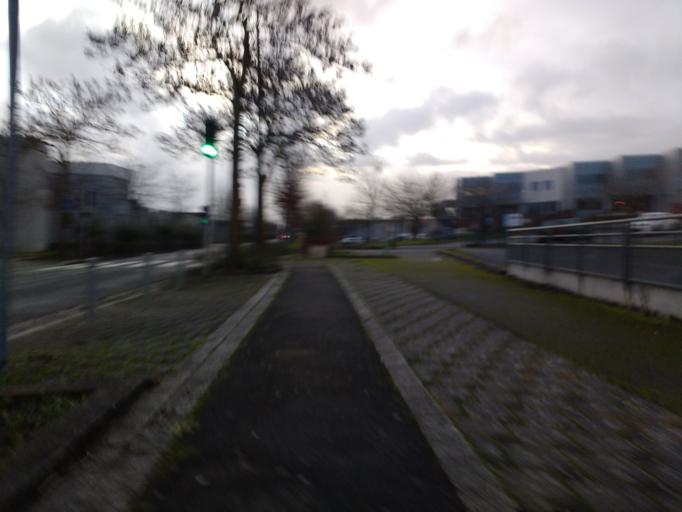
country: FR
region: Picardie
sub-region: Departement de la Somme
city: Longueau
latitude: 49.8676
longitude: 2.3647
